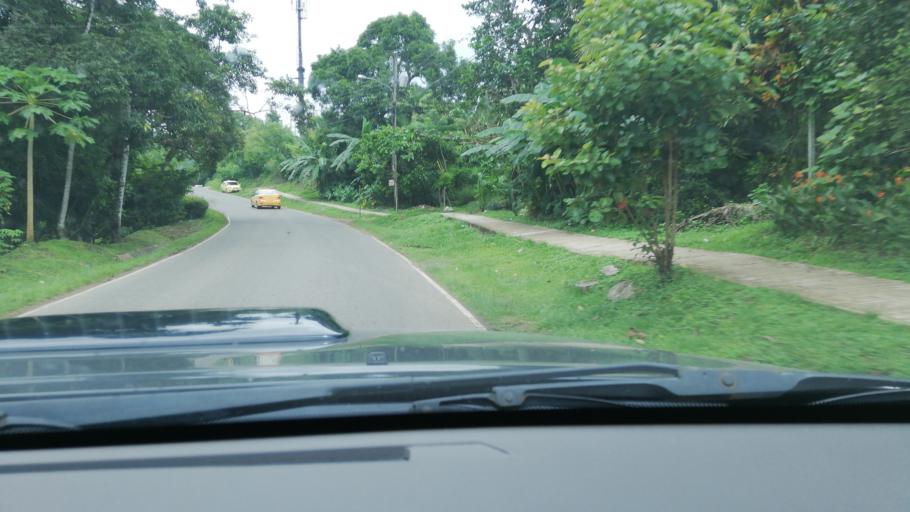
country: PA
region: Panama
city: San Miguelito
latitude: 9.1021
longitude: -79.4470
